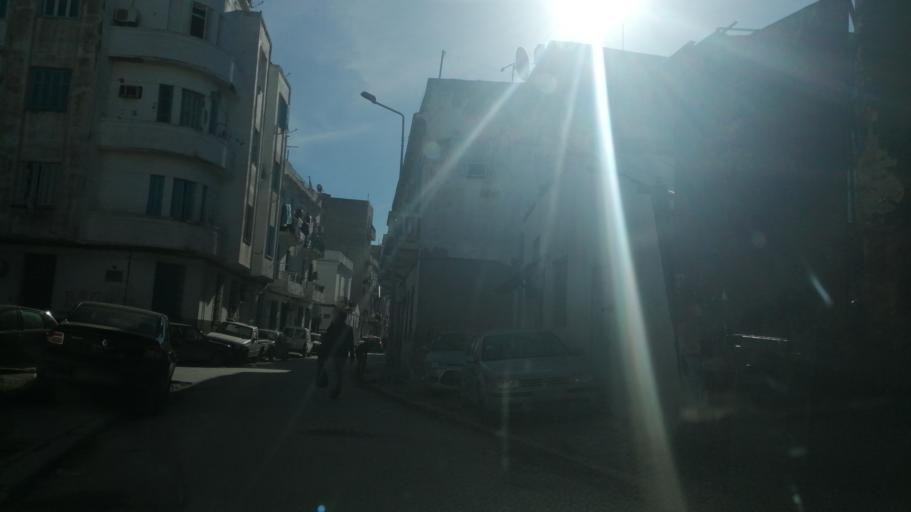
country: TN
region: Tunis
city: Tunis
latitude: 36.8107
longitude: 10.1762
